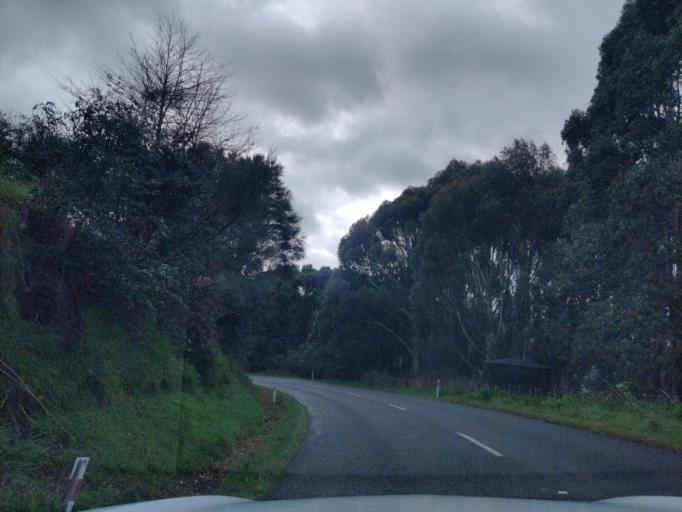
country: NZ
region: Manawatu-Wanganui
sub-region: Palmerston North City
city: Palmerston North
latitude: -40.1824
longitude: 175.7887
